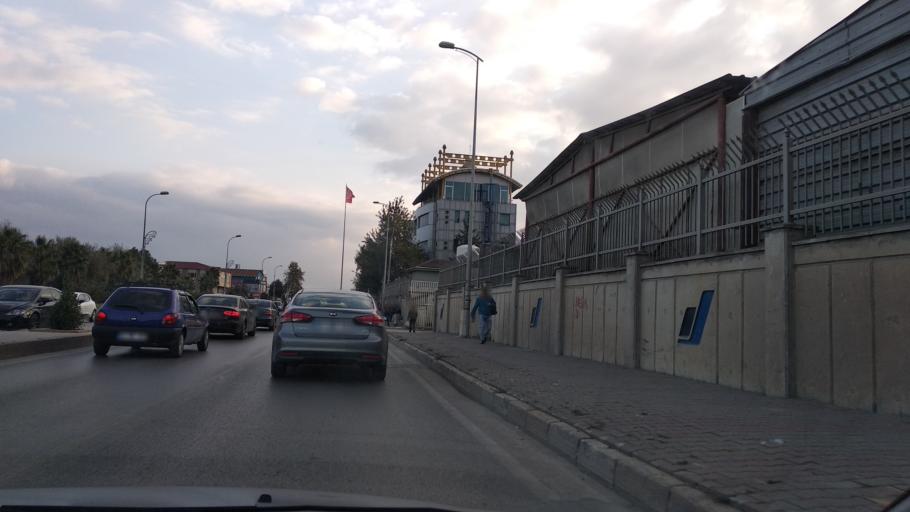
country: TR
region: Istanbul
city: Icmeler
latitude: 40.8456
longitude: 29.2933
